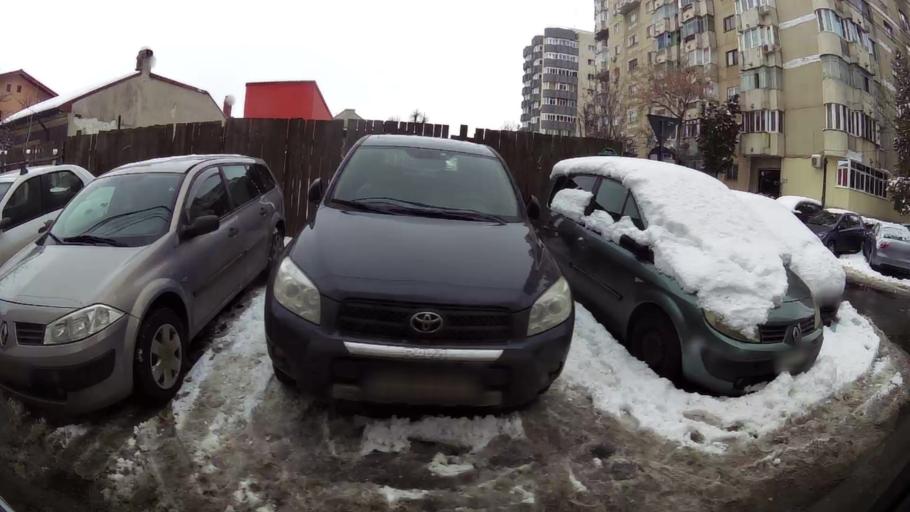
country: RO
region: Bucuresti
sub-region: Municipiul Bucuresti
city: Bucuresti
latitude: 44.3996
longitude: 26.0992
